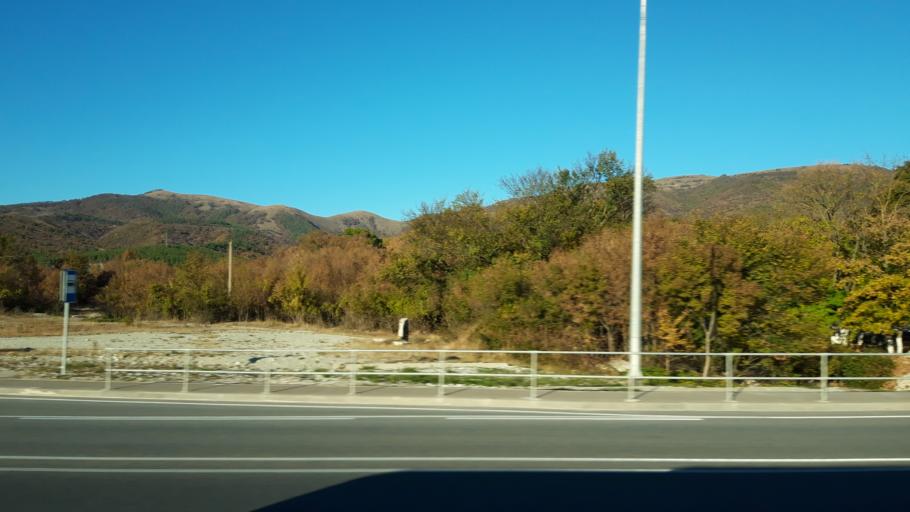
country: RU
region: Krasnodarskiy
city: Kabardinka
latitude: 44.6342
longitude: 37.9968
